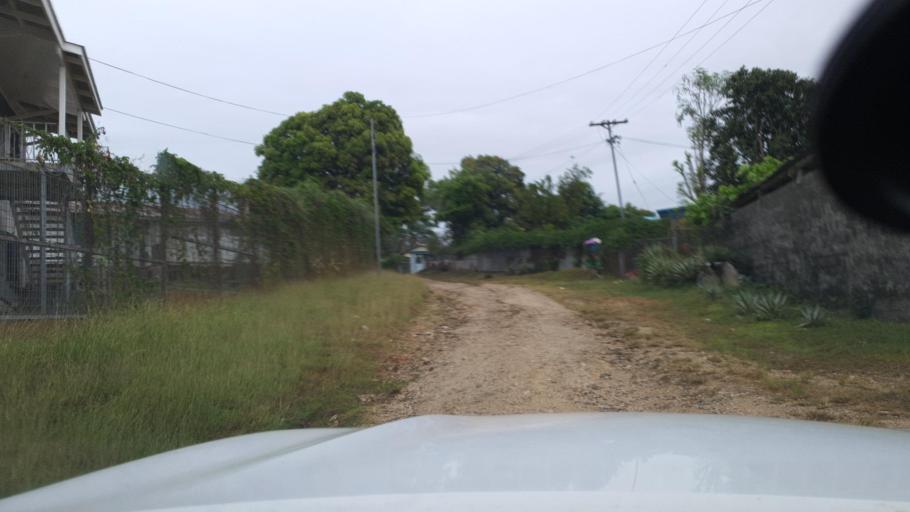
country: SB
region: Guadalcanal
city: Honiara
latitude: -9.4411
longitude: 159.9669
